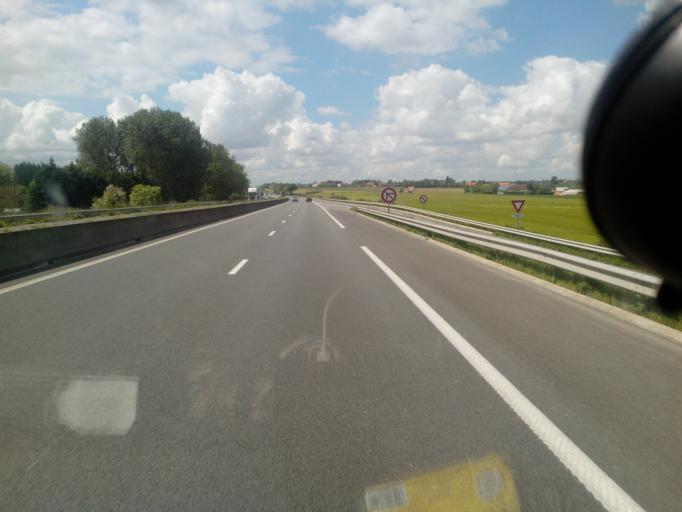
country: FR
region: Nord-Pas-de-Calais
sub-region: Departement du Nord
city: Meteren
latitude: 50.7444
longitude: 2.6760
